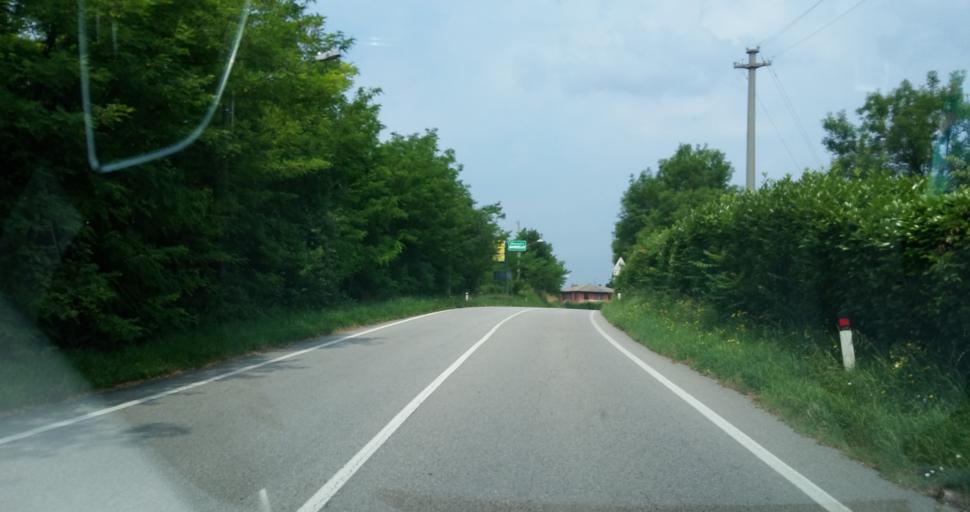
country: IT
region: Lombardy
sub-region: Provincia di Varese
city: Bardello
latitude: 45.8320
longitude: 8.7048
